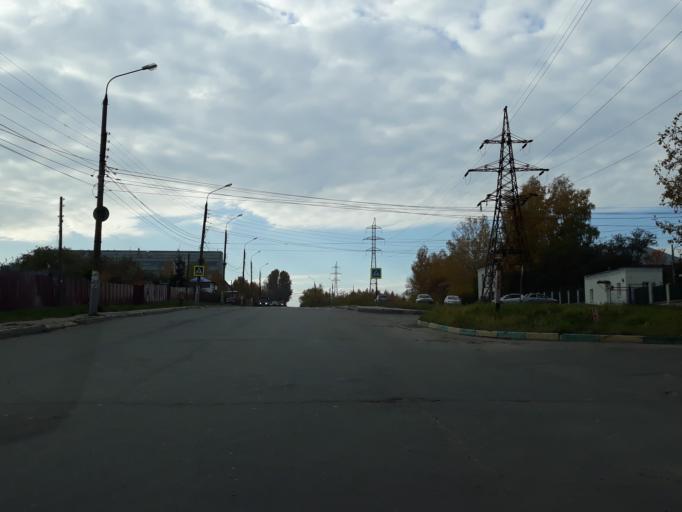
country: RU
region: Nizjnij Novgorod
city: Nizhniy Novgorod
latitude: 56.2441
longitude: 43.9807
